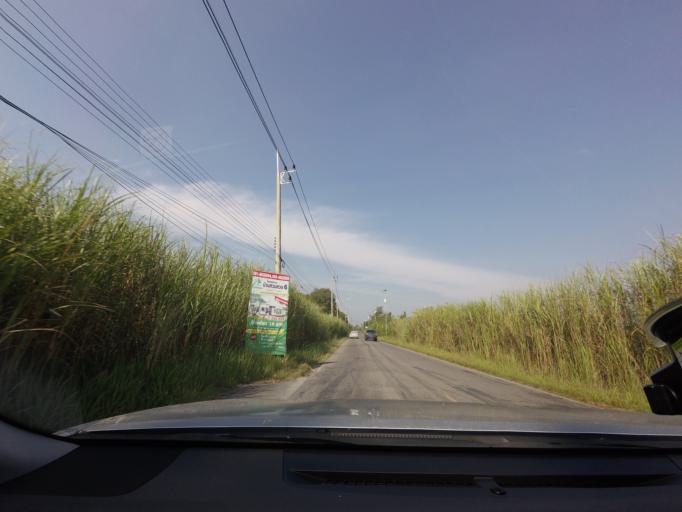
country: TH
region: Nakhon Si Thammarat
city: Nakhon Si Thammarat
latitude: 8.5119
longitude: 99.9670
